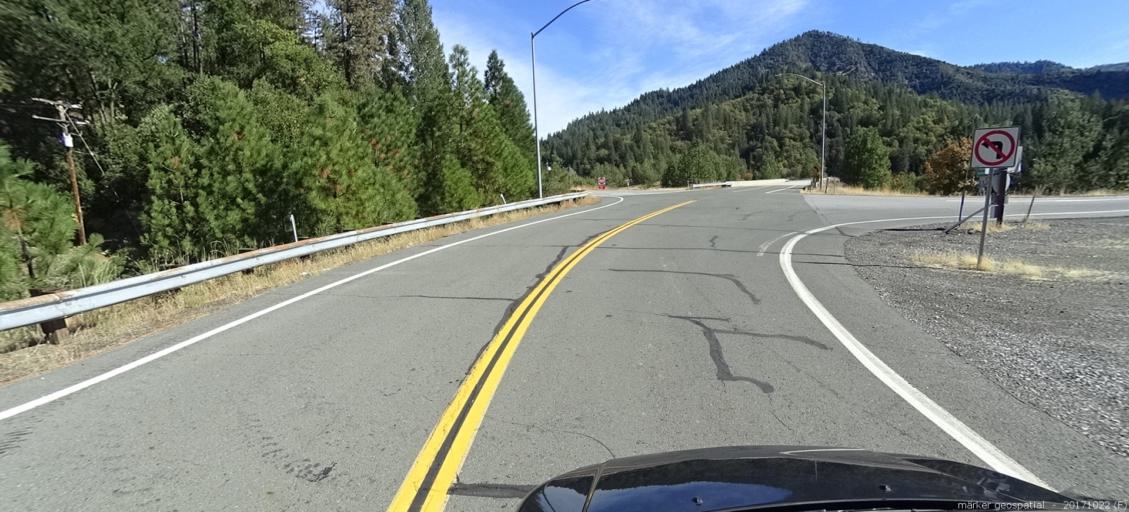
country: US
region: California
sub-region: Siskiyou County
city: Dunsmuir
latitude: 40.9785
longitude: -122.4336
